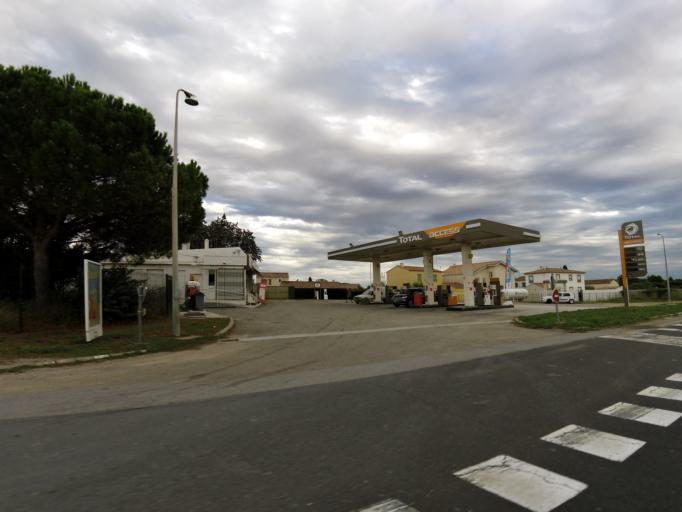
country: FR
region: Languedoc-Roussillon
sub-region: Departement du Gard
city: Aimargues
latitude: 43.6960
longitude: 4.2006
